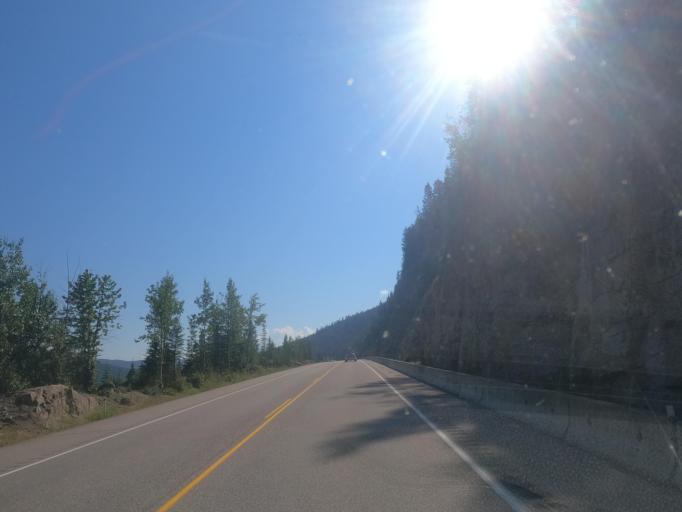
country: CA
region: Alberta
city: Jasper Park Lodge
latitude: 52.8743
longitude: -118.3087
